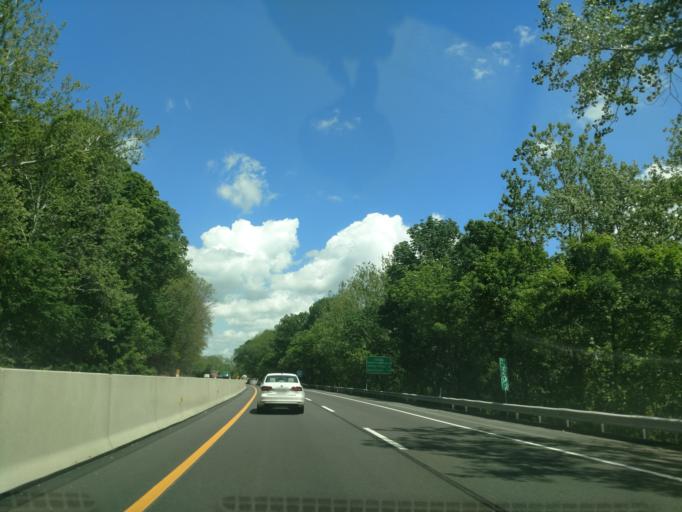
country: US
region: Pennsylvania
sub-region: Chester County
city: Malvern
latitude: 40.0734
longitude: -75.5217
